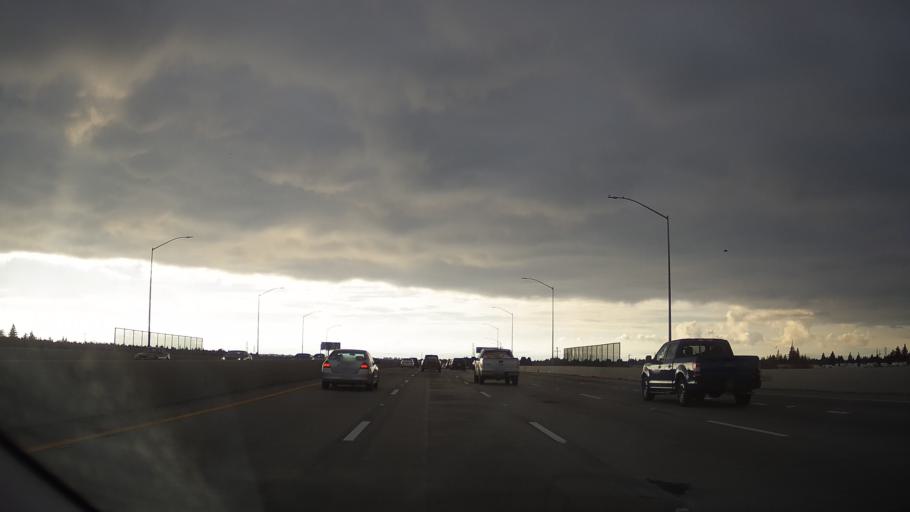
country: US
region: California
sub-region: Sacramento County
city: Rio Linda
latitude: 38.6415
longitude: -121.4706
